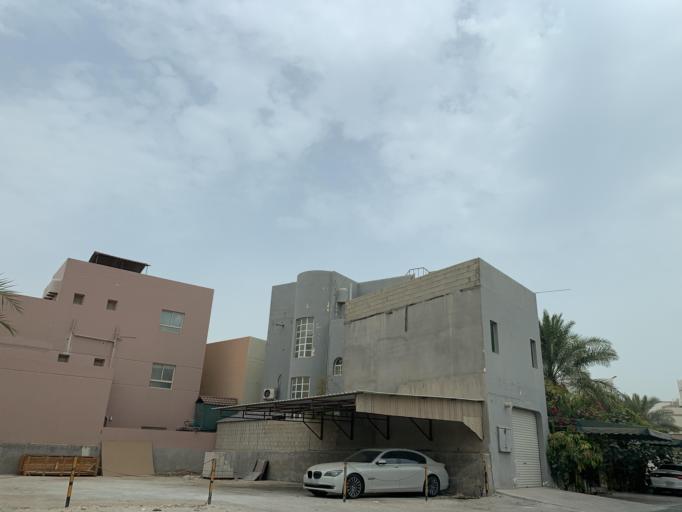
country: BH
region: Northern
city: Madinat `Isa
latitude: 26.1823
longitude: 50.4768
